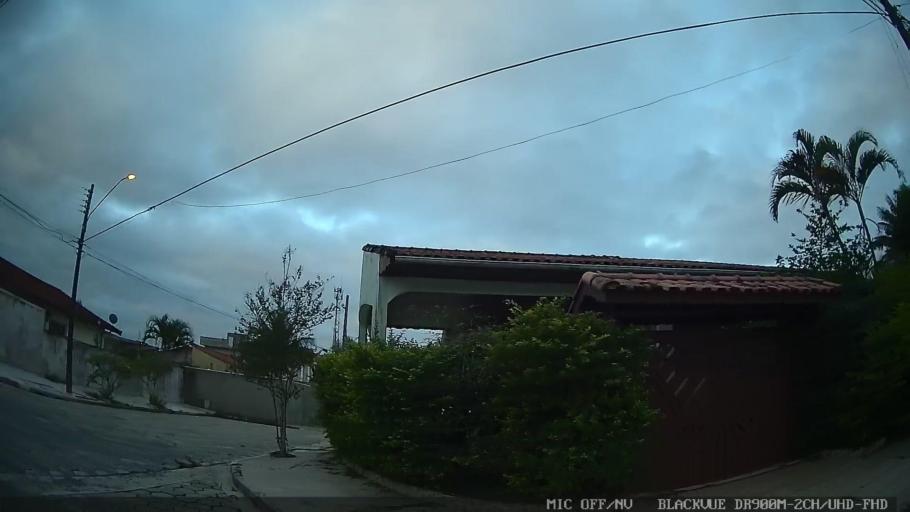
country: BR
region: Sao Paulo
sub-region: Peruibe
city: Peruibe
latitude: -24.3057
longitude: -46.9821
